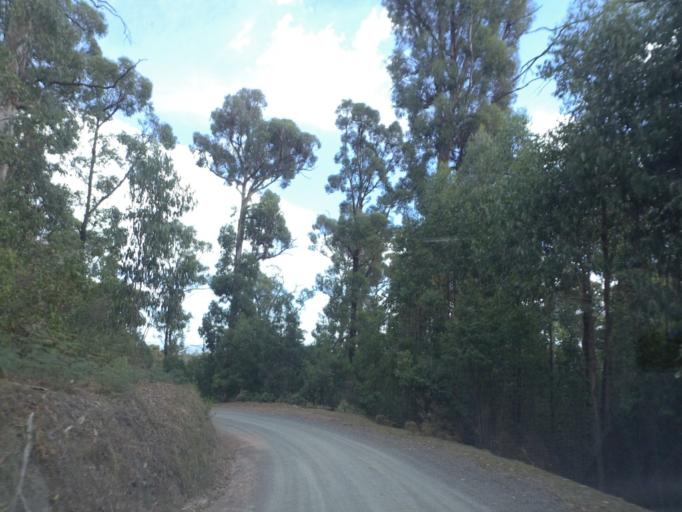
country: AU
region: Victoria
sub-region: Murrindindi
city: Alexandra
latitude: -37.4199
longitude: 145.7599
